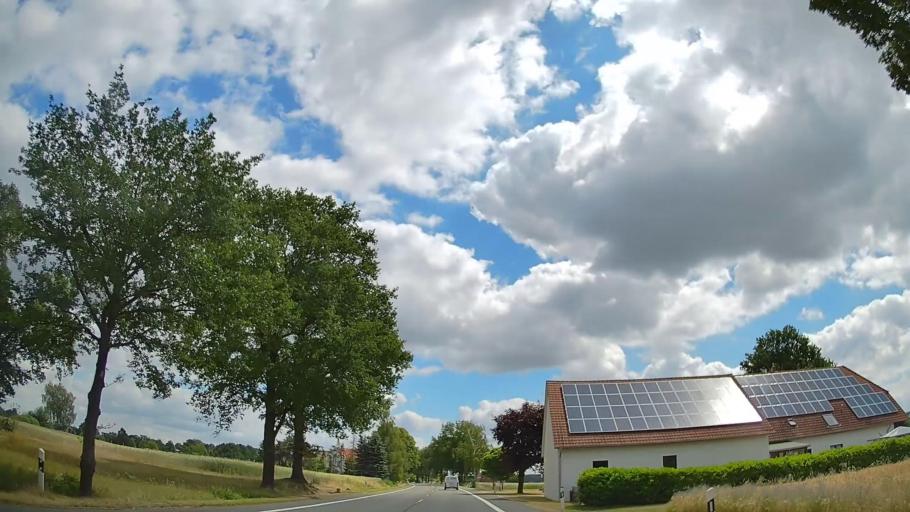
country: DE
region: North Rhine-Westphalia
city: Espelkamp
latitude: 52.3909
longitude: 8.5371
